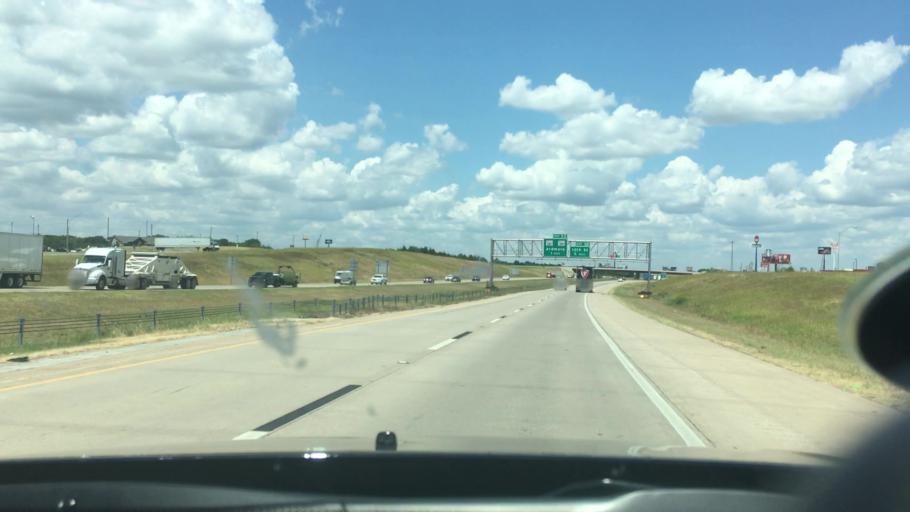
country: US
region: Oklahoma
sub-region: Carter County
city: Ardmore
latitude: 34.1812
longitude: -97.1677
